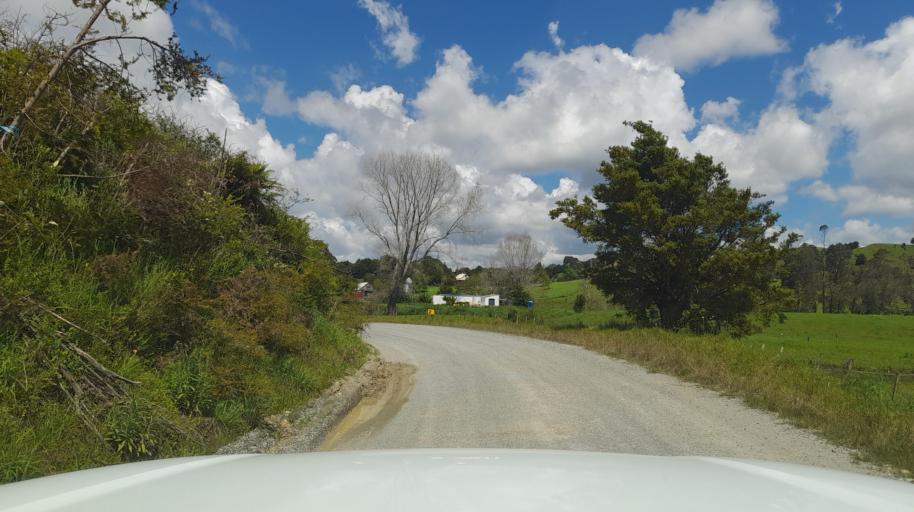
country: NZ
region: Northland
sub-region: Far North District
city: Kaitaia
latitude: -35.1203
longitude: 173.3984
